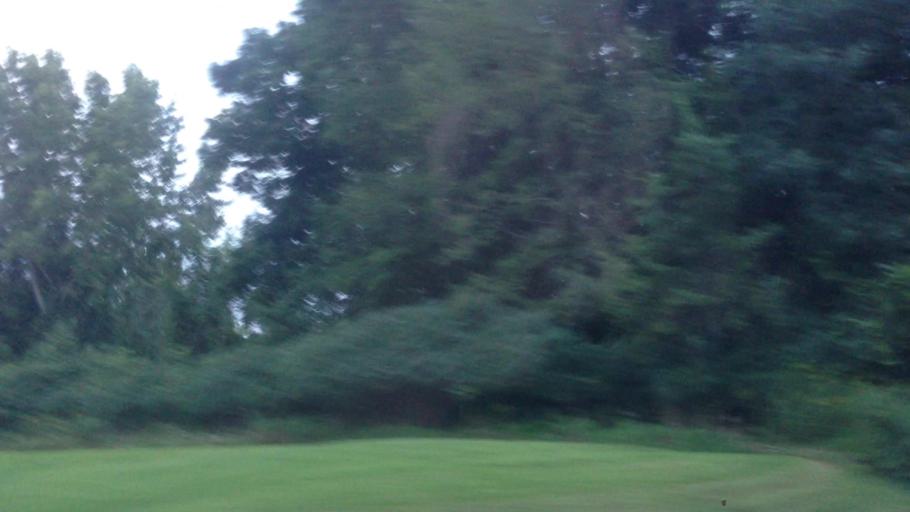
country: US
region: New York
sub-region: Dutchess County
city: Red Hook
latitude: 41.9979
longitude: -73.8873
